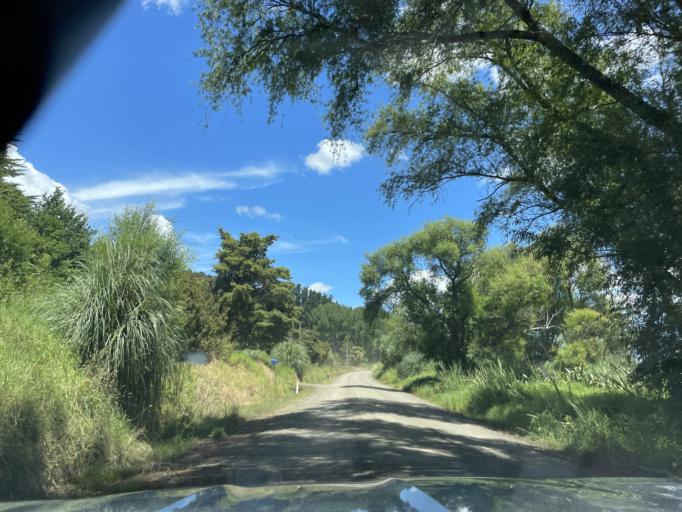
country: NZ
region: Northland
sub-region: Kaipara District
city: Dargaville
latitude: -35.9079
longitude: 173.9226
